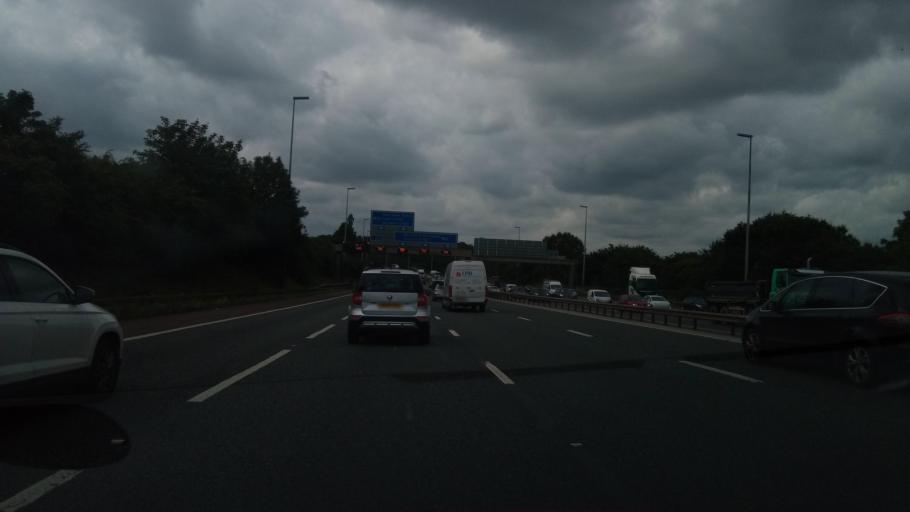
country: GB
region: England
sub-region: Lancashire
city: Clayton-le-Woods
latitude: 53.7478
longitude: -2.6467
